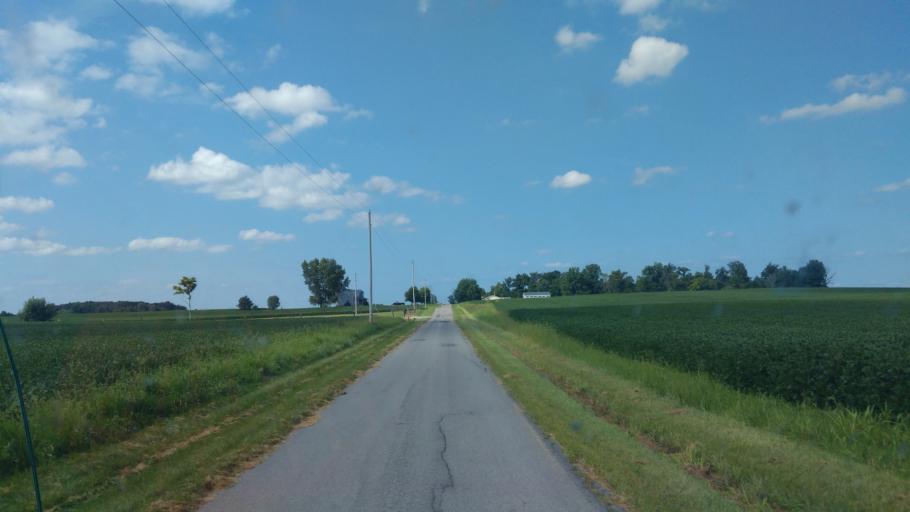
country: US
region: Ohio
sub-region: Union County
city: Richwood
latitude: 40.5075
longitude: -83.4508
